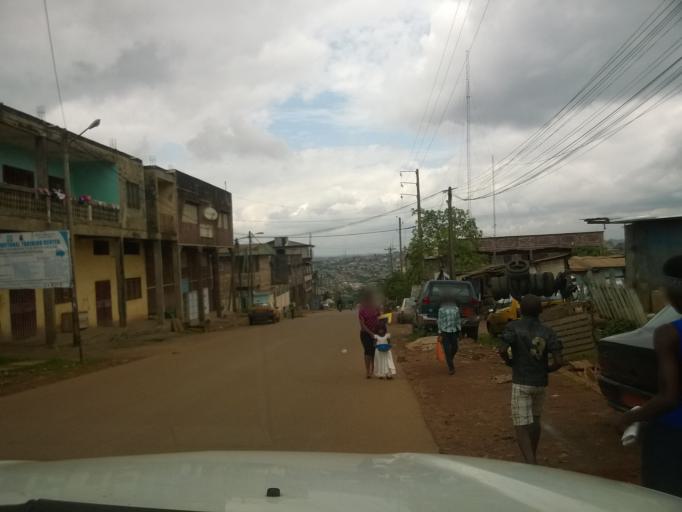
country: CM
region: Centre
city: Yaounde
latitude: 3.8362
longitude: 11.4765
